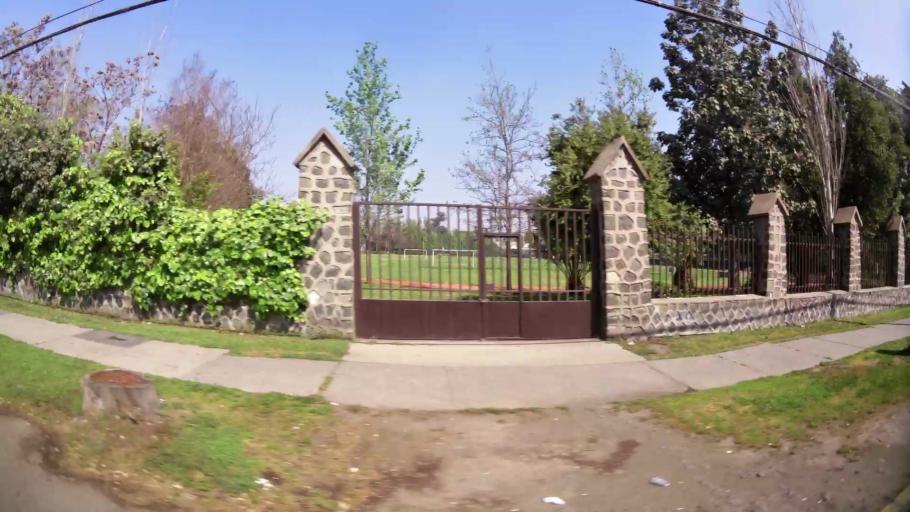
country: CL
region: Santiago Metropolitan
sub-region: Provincia de Santiago
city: Lo Prado
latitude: -33.4443
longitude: -70.6860
